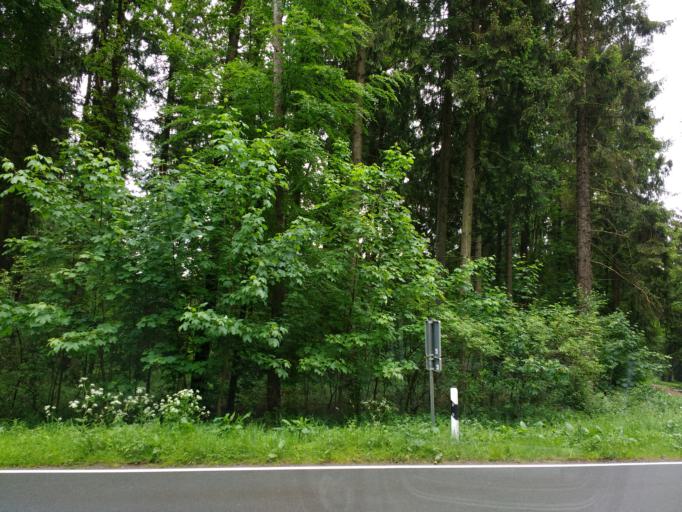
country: DE
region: Lower Saxony
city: Georgsmarienhutte
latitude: 52.1774
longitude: 8.0886
